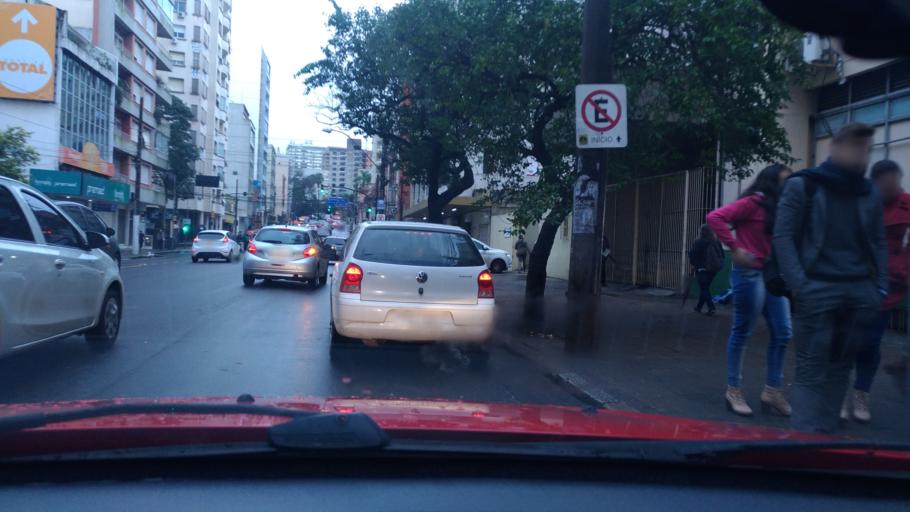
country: BR
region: Rio Grande do Sul
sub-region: Porto Alegre
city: Porto Alegre
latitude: -30.0294
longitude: -51.2147
